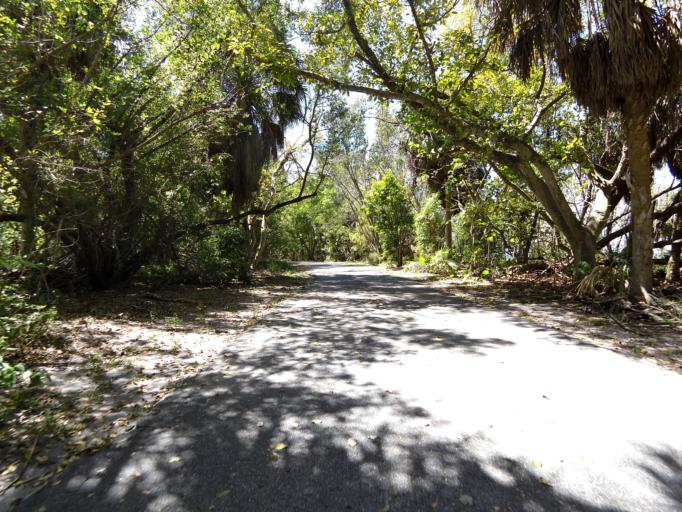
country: US
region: Florida
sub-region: Miami-Dade County
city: Key Biscayne
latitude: 25.6733
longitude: -80.1618
